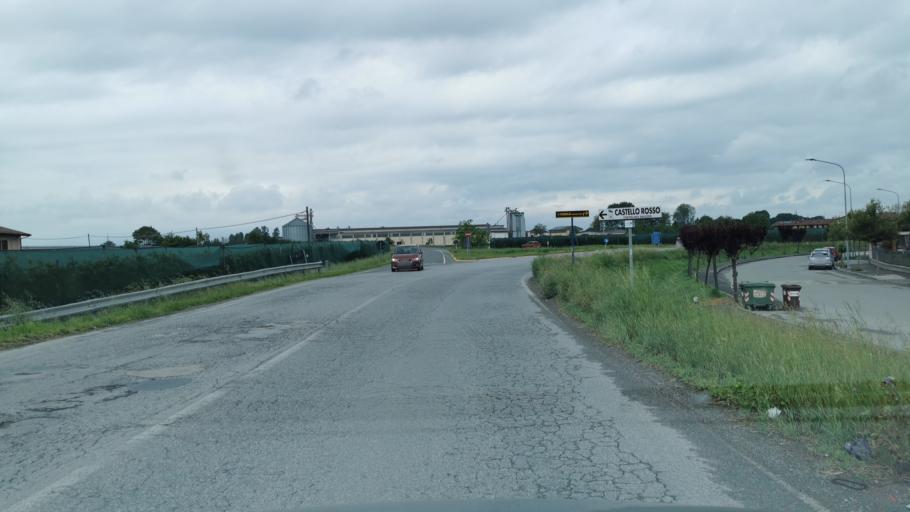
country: IT
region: Piedmont
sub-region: Provincia di Cuneo
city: Savigliano
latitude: 44.6407
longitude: 7.6474
